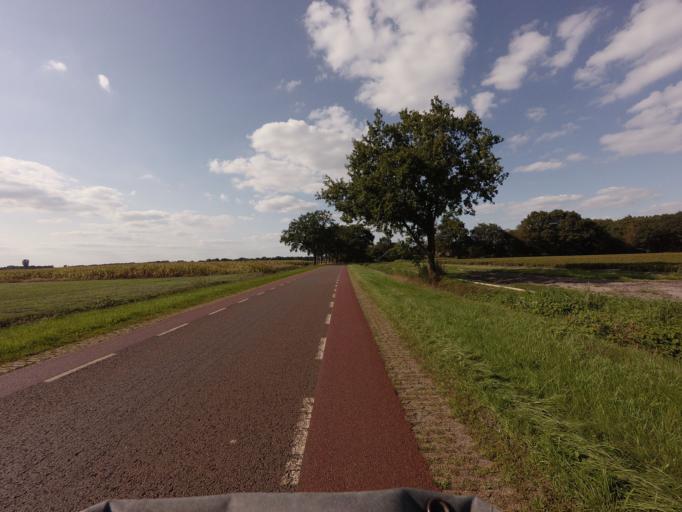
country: NL
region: Drenthe
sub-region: Gemeente Westerveld
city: Dwingeloo
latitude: 52.8468
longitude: 6.3968
